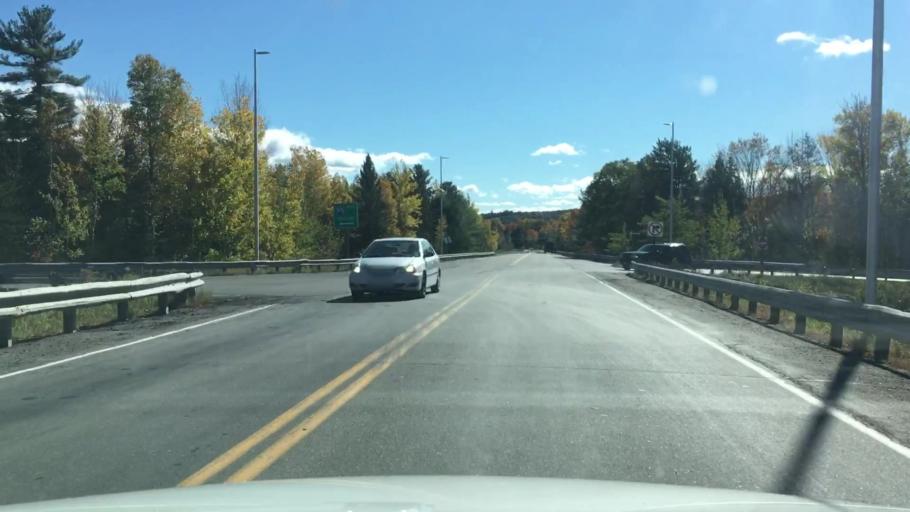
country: US
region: Maine
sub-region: Penobscot County
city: Medway
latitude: 45.6063
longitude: -68.5217
